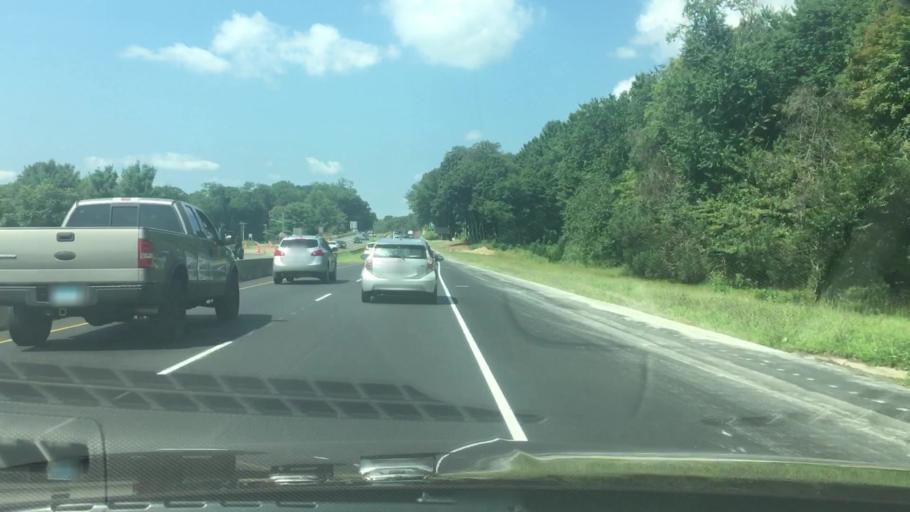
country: US
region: Connecticut
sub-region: Fairfield County
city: Westport
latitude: 41.1645
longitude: -73.3716
